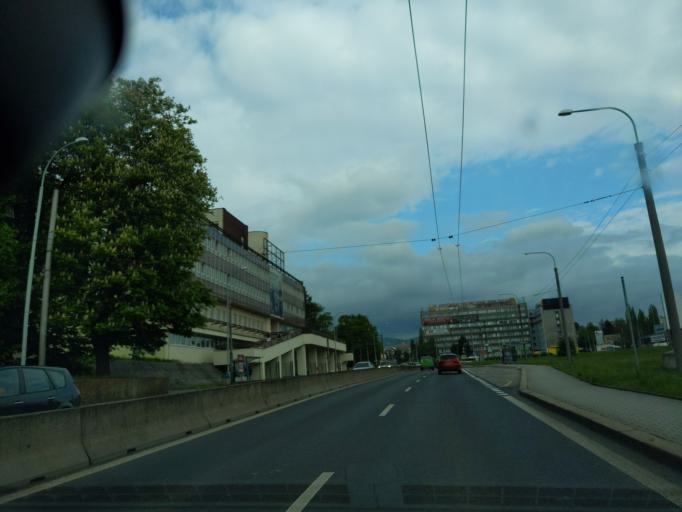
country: CZ
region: Ustecky
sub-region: Okres Usti nad Labem
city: Usti nad Labem
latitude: 50.6788
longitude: 14.0099
